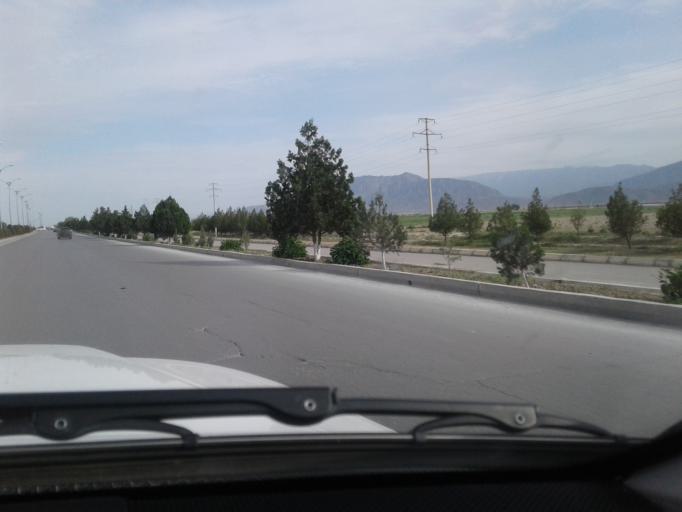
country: TM
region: Ahal
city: Abadan
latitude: 38.1525
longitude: 57.9788
